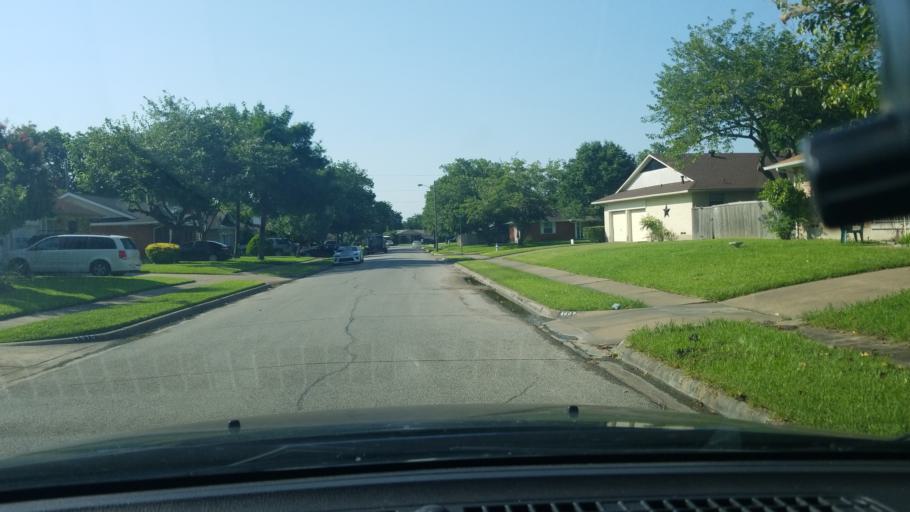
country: US
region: Texas
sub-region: Dallas County
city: Mesquite
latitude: 32.8282
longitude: -96.6400
